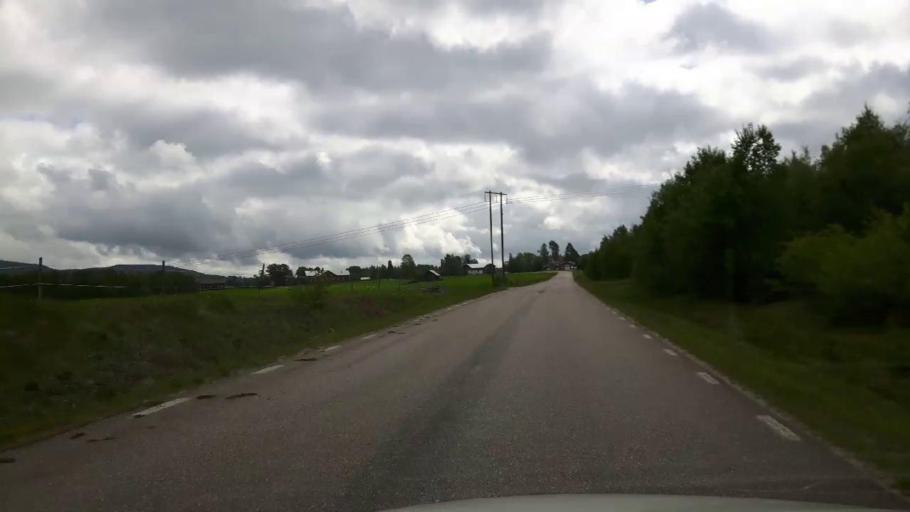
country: SE
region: Gaevleborg
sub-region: Ovanakers Kommun
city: Edsbyn
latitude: 61.3569
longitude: 15.9022
